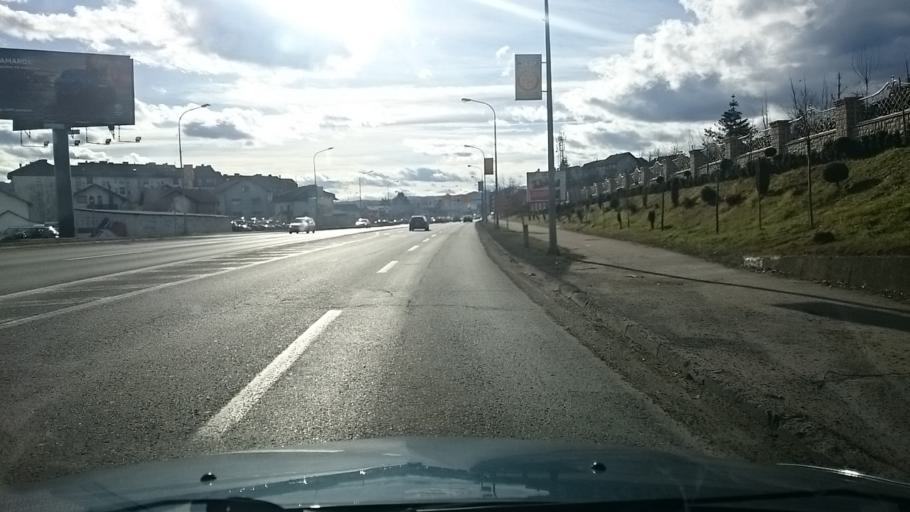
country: BA
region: Republika Srpska
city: Banja Luka
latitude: 44.7876
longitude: 17.1978
